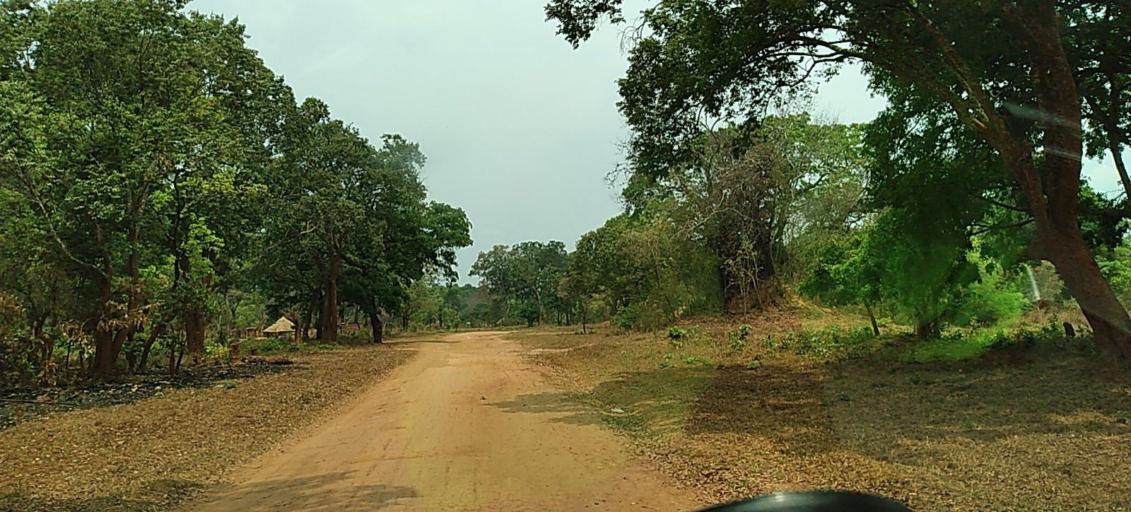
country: ZM
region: North-Western
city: Solwezi
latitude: -12.8022
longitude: 26.5363
